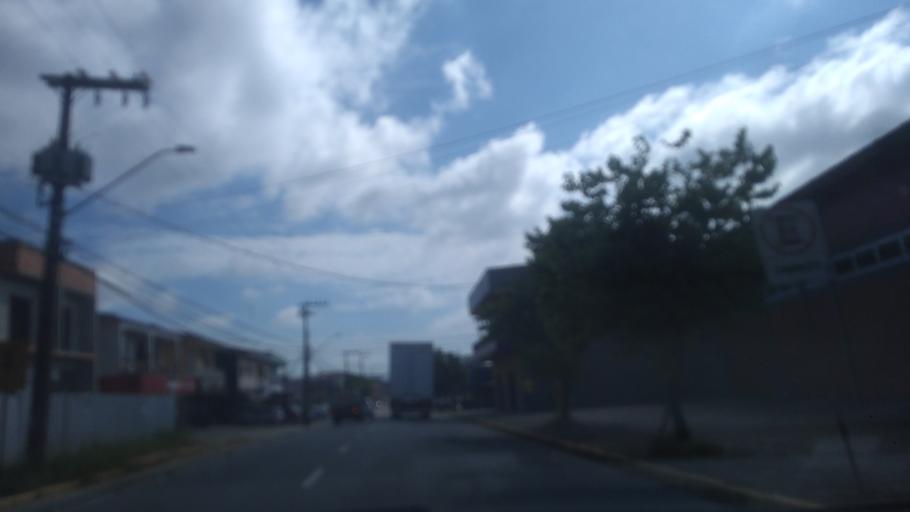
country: BR
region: Santa Catarina
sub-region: Joinville
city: Joinville
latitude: -26.2982
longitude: -48.8201
